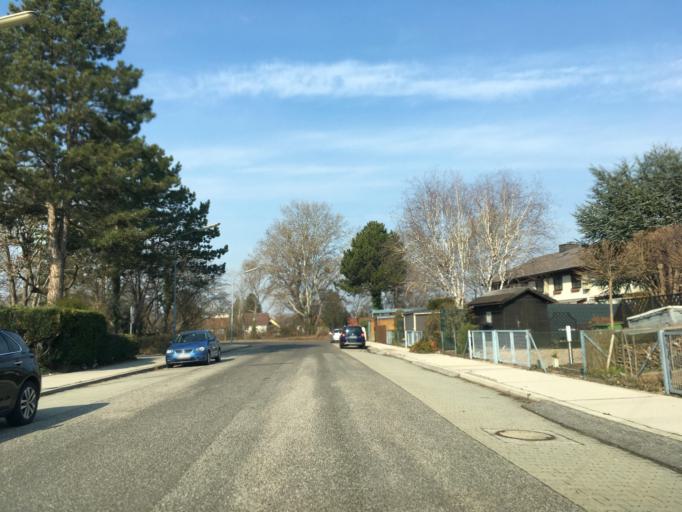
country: AT
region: Lower Austria
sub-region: Politischer Bezirk Ganserndorf
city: Gross-Enzersdorf
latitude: 48.2101
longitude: 16.4743
